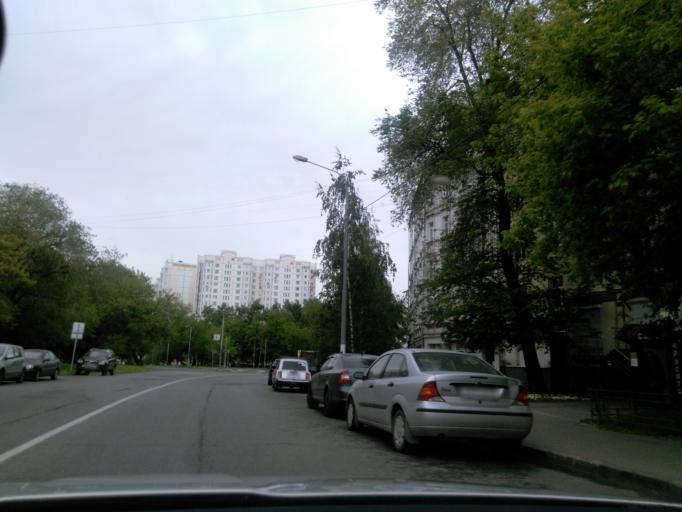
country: RU
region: Moscow
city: Taganskiy
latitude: 55.7374
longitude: 37.6755
